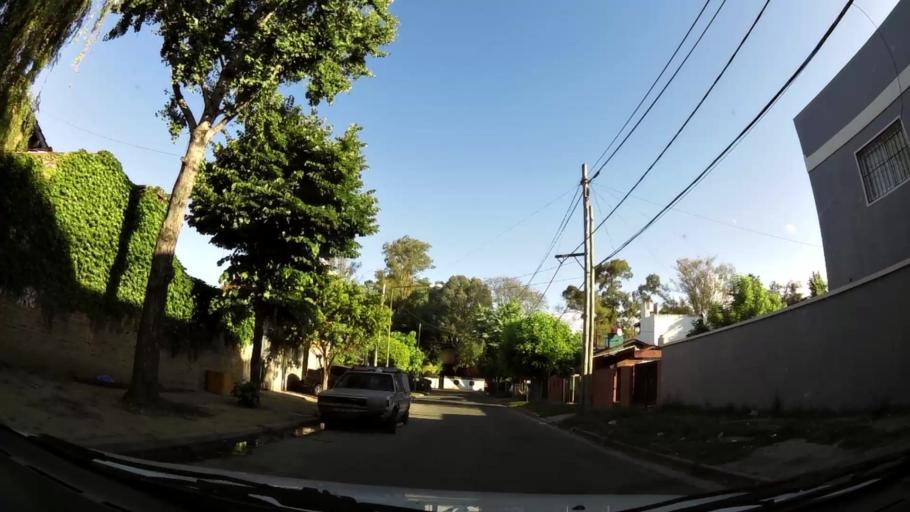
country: AR
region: Buenos Aires
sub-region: Partido de San Isidro
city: San Isidro
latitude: -34.4753
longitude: -58.5525
